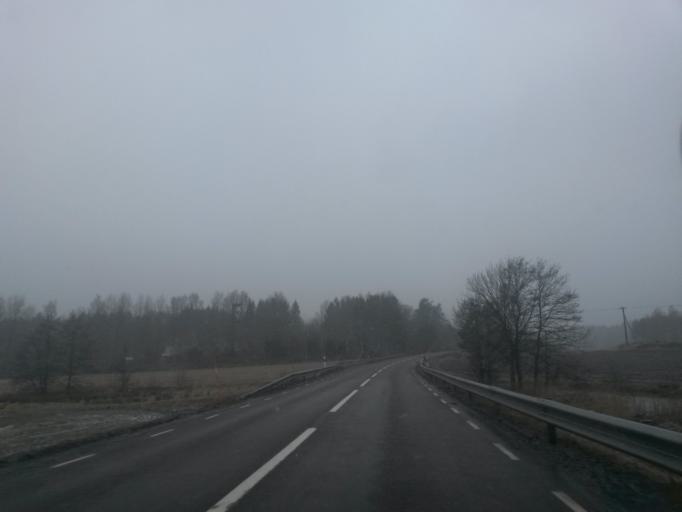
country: SE
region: Vaestra Goetaland
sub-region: Vanersborgs Kommun
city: Vargon
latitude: 58.2196
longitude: 12.4254
